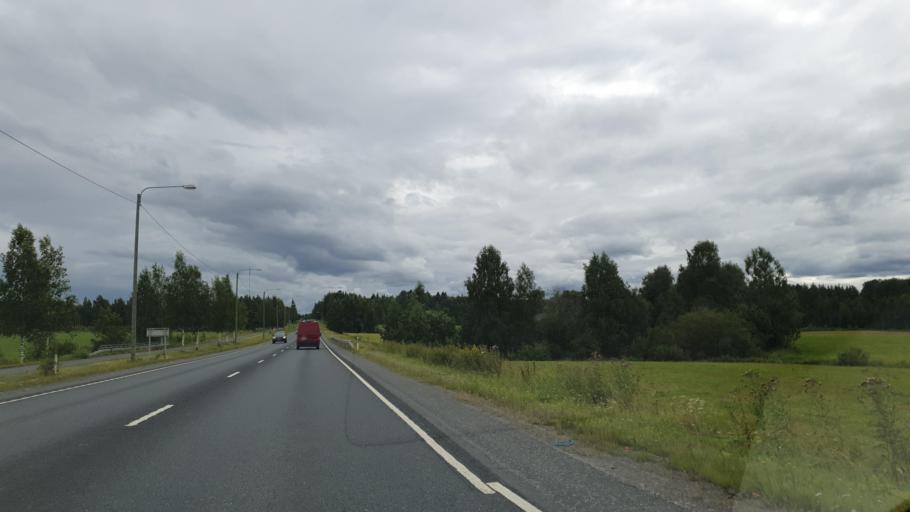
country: FI
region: Northern Savo
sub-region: Ylae-Savo
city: Lapinlahti
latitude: 63.4382
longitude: 27.3255
